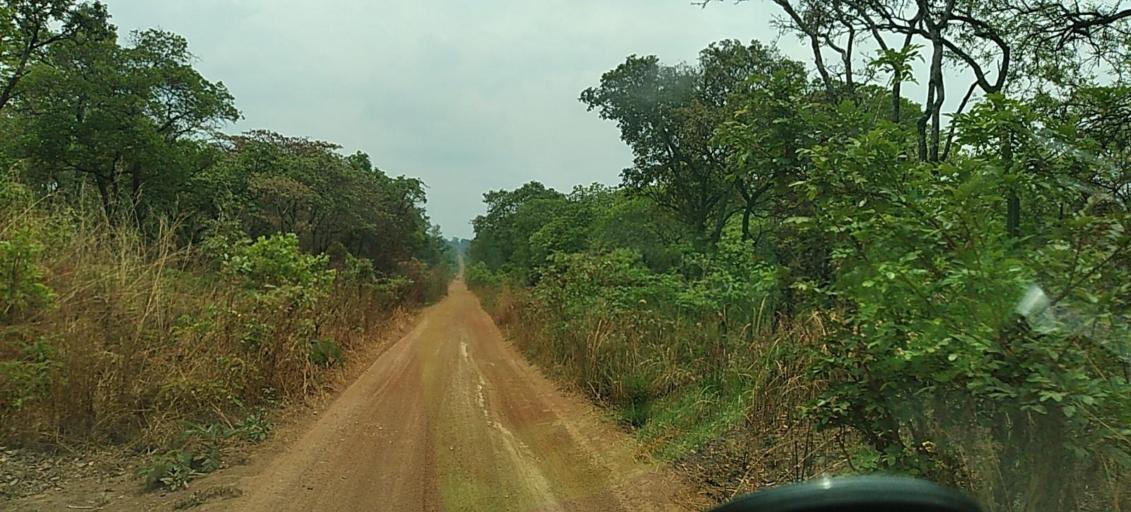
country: ZM
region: North-Western
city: Kansanshi
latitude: -12.0336
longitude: 26.3173
